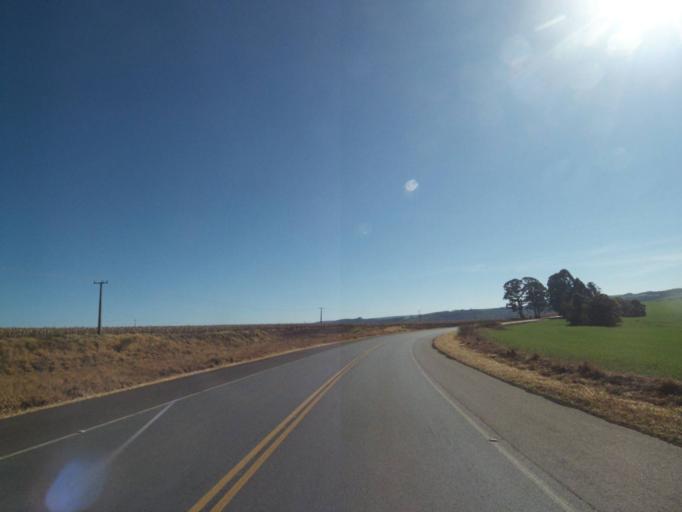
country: BR
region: Parana
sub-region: Tibagi
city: Tibagi
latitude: -24.3930
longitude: -50.3363
